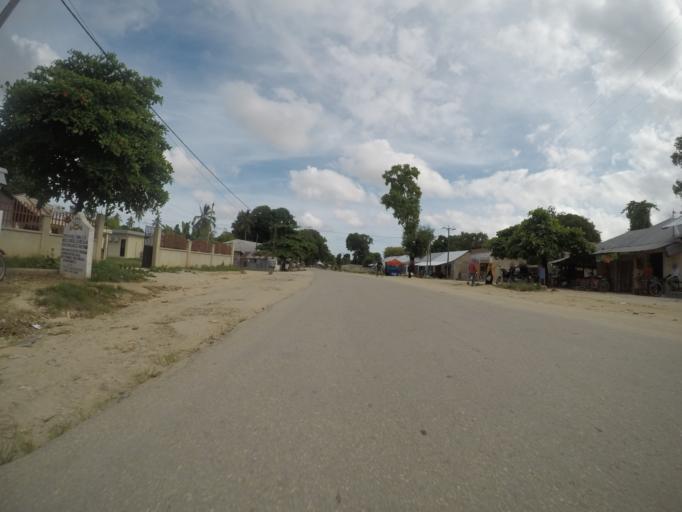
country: TZ
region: Pemba South
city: Chake Chake
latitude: -5.2396
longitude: 39.7808
